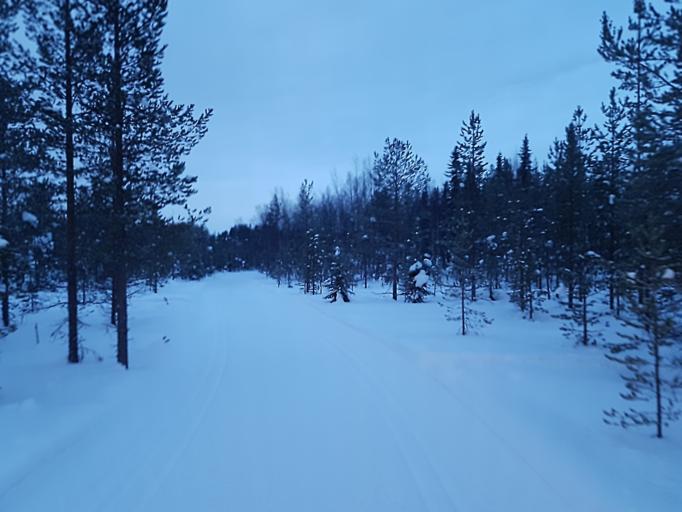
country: FI
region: Lapland
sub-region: Tunturi-Lappi
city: Kolari
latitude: 67.6211
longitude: 24.1409
